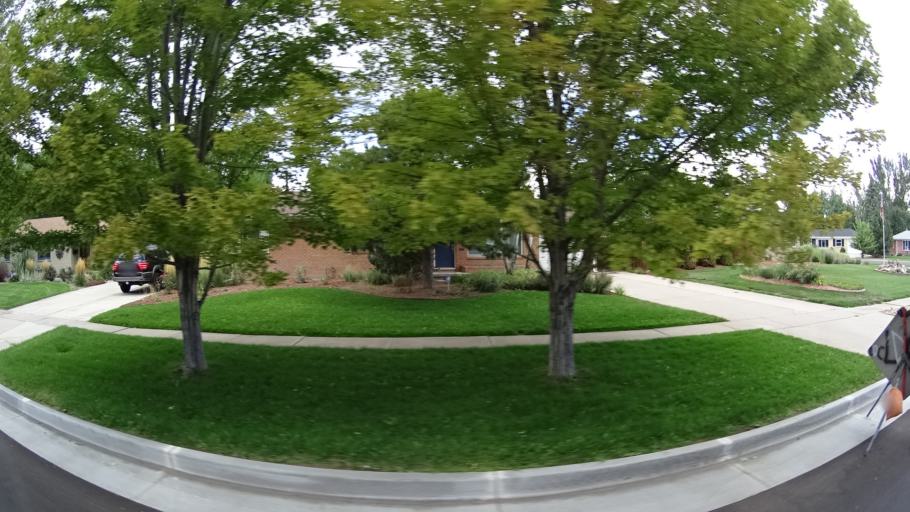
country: US
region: Colorado
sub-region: El Paso County
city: Colorado Springs
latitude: 38.8634
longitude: -104.8073
